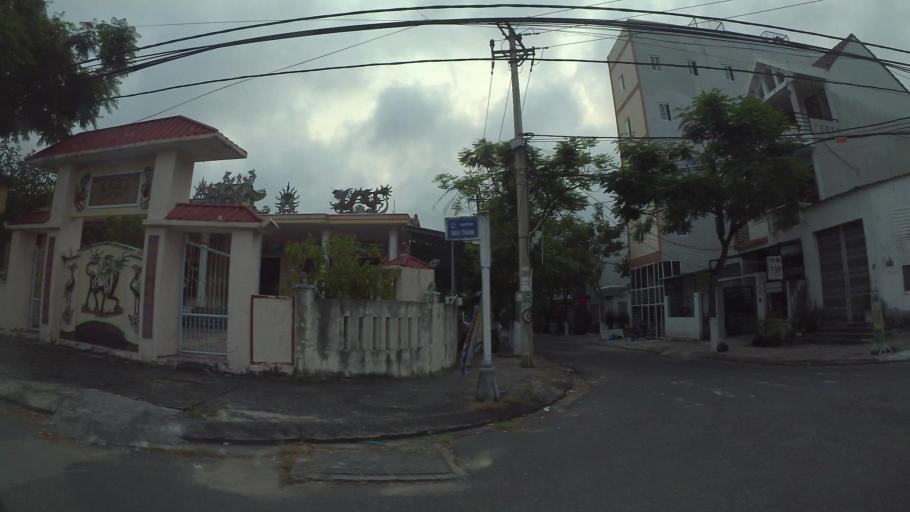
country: VN
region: Da Nang
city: Son Tra
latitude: 16.0404
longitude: 108.2401
